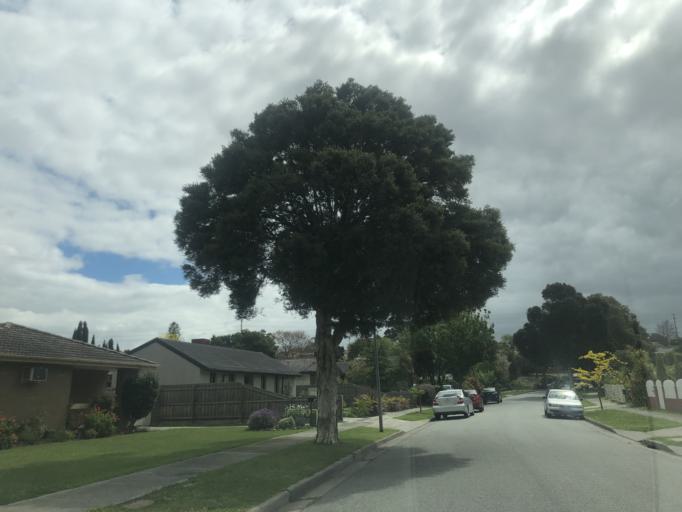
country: AU
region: Victoria
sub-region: Casey
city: Endeavour Hills
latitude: -37.9758
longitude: 145.2439
